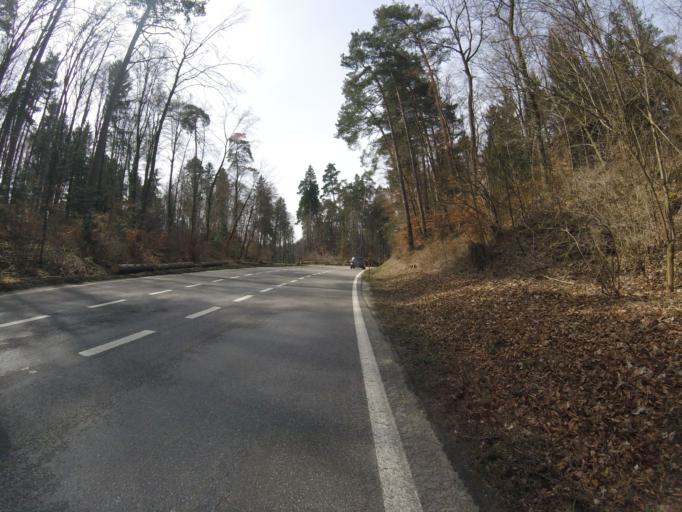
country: CH
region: Fribourg
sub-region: Sense District
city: Bosingen
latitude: 46.9071
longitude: 7.2119
